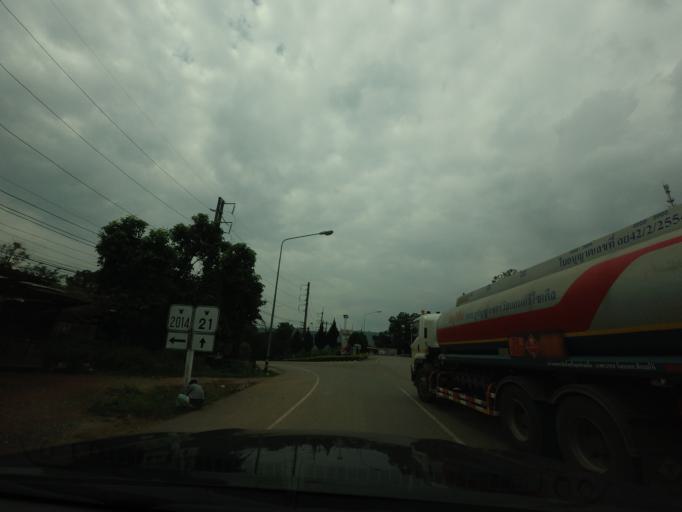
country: TH
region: Loei
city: Dan Sai
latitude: 17.2054
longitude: 101.1595
